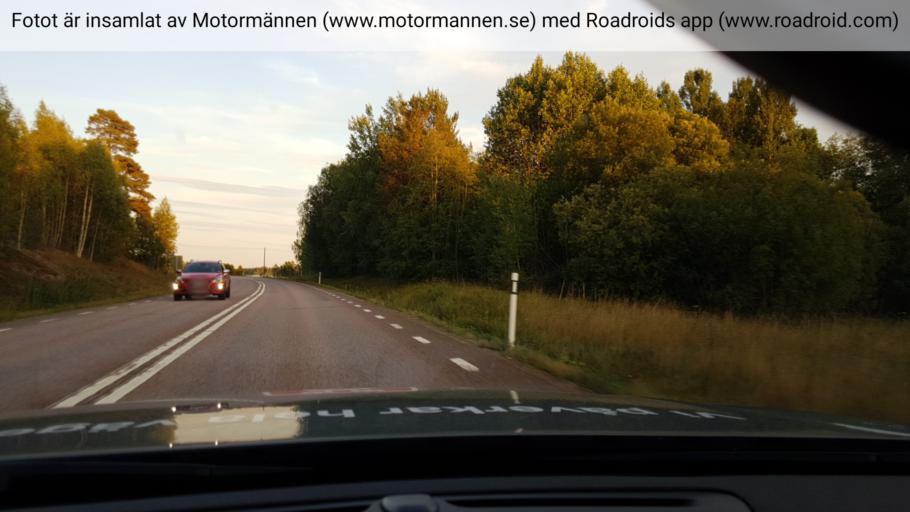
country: SE
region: OErebro
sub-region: Karlskoga Kommun
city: Karlskoga
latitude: 59.4006
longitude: 14.4337
